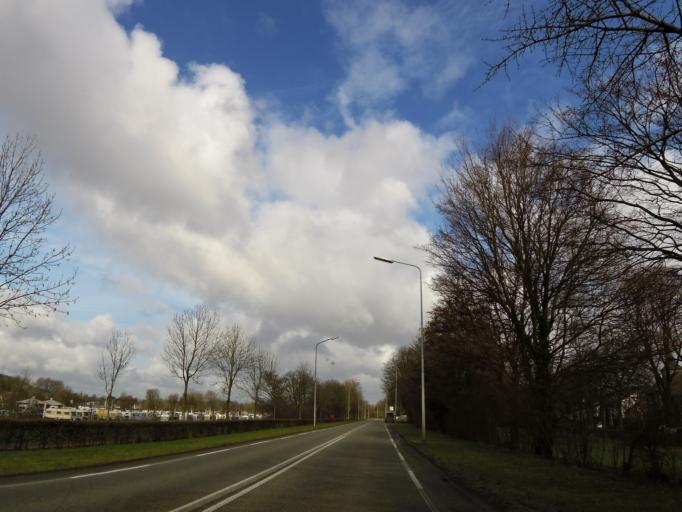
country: NL
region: Limburg
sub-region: Gemeente Maastricht
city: Maastricht
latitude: 50.8277
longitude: 5.7028
